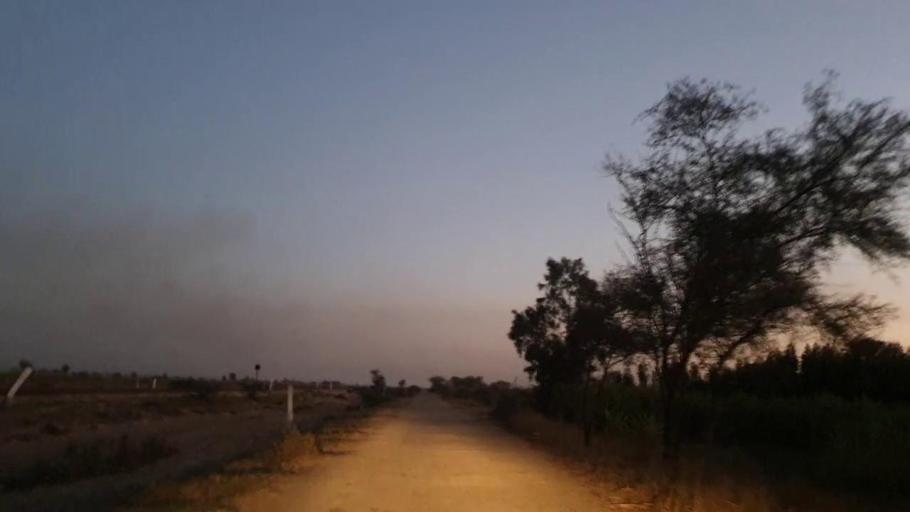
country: PK
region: Sindh
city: Nawabshah
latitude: 26.3394
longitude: 68.3715
